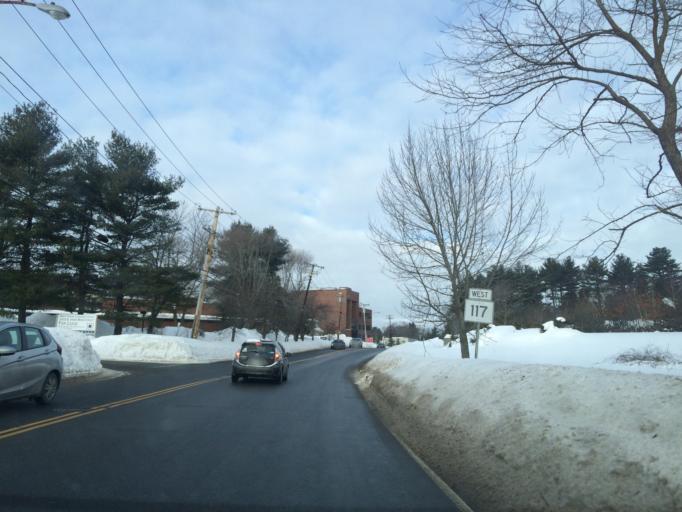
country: US
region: Massachusetts
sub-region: Middlesex County
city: Weston
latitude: 42.3770
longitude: -71.2713
